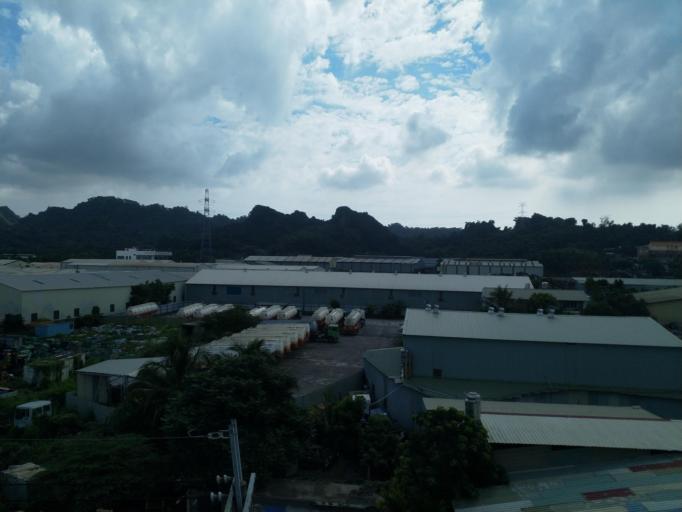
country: TW
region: Taiwan
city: Fengshan
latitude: 22.7230
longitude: 120.3600
